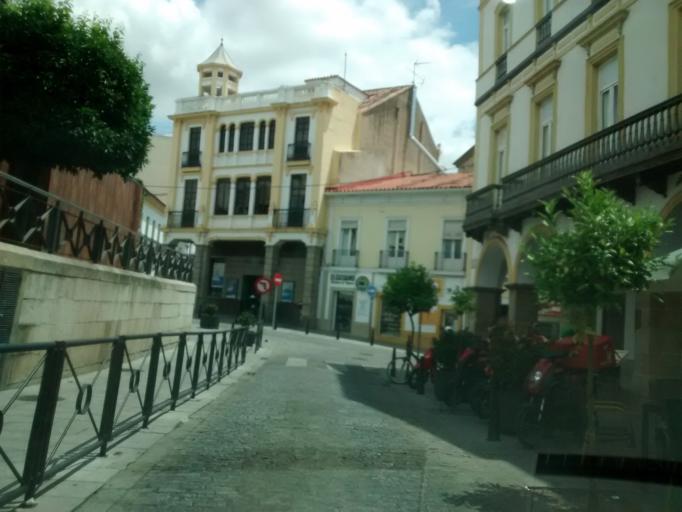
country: ES
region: Extremadura
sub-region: Provincia de Badajoz
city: Merida
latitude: 38.9162
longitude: -6.3467
